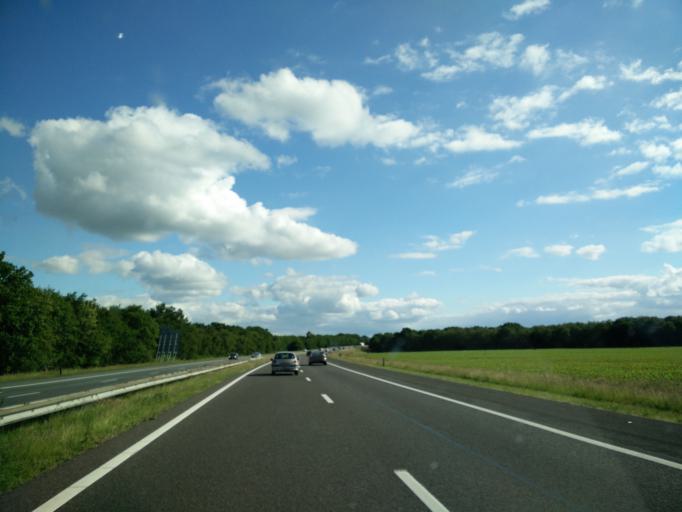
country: NL
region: Drenthe
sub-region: Gemeente Tynaarlo
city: Tynaarlo
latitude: 53.0684
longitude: 6.6039
